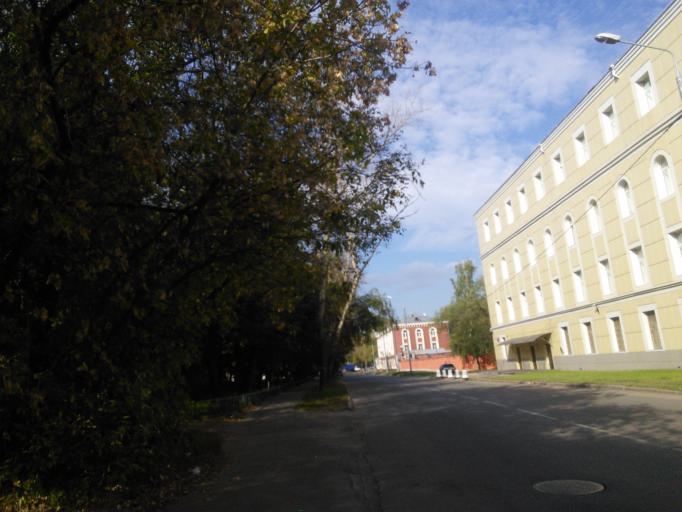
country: RU
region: Moscow
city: Mar'ina Roshcha
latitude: 55.8085
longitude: 37.5896
